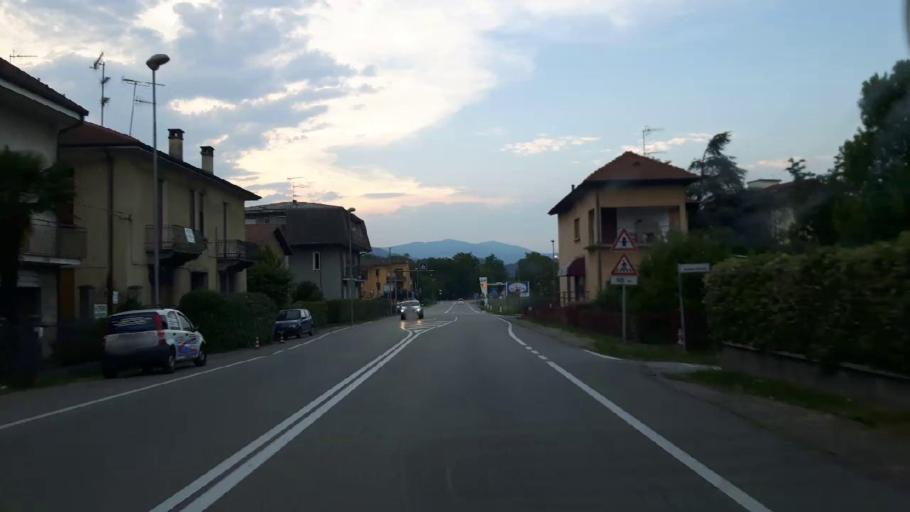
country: IT
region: Piedmont
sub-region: Provincia di Novara
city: Dormelletto
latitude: 45.7437
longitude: 8.5666
